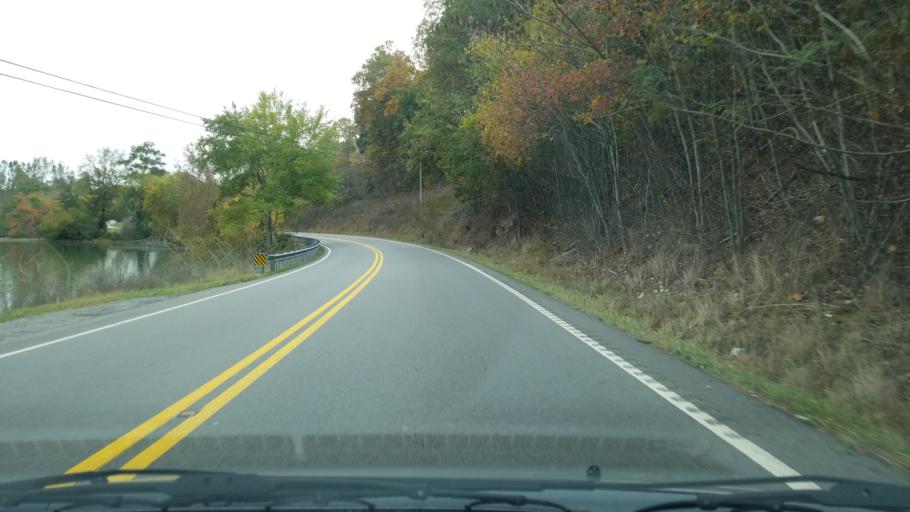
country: US
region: Tennessee
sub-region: Bradley County
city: Hopewell
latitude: 35.3377
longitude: -84.9713
